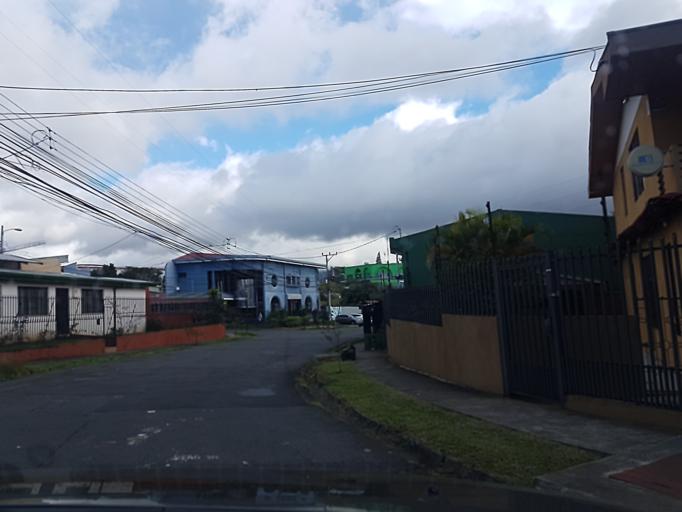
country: CR
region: San Jose
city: San Pedro
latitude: 9.9240
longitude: -84.0601
